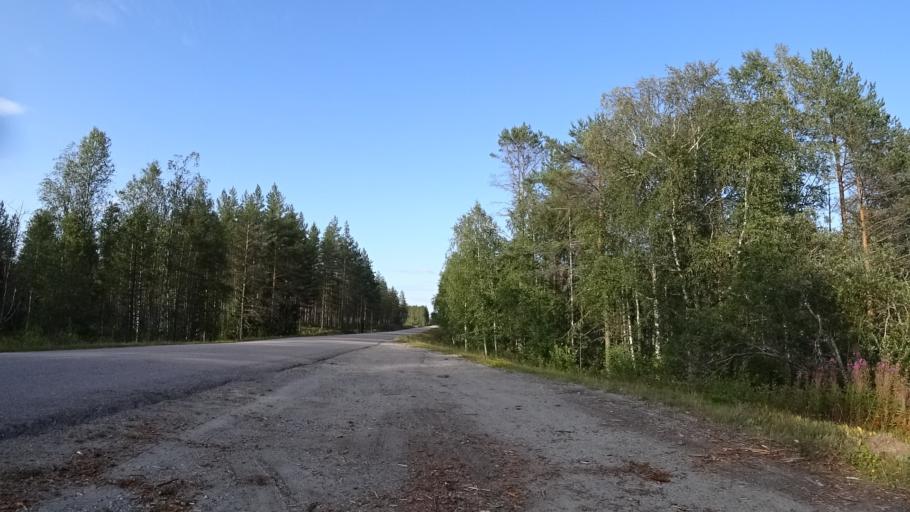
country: FI
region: North Karelia
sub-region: Joensuu
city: Eno
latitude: 63.0787
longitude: 30.5815
